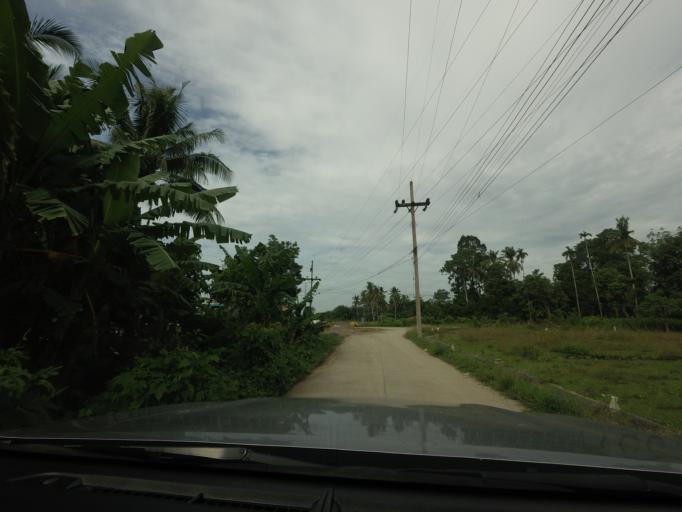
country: TH
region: Nakhon Si Thammarat
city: Phra Phrom
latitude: 8.2824
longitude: 99.9114
